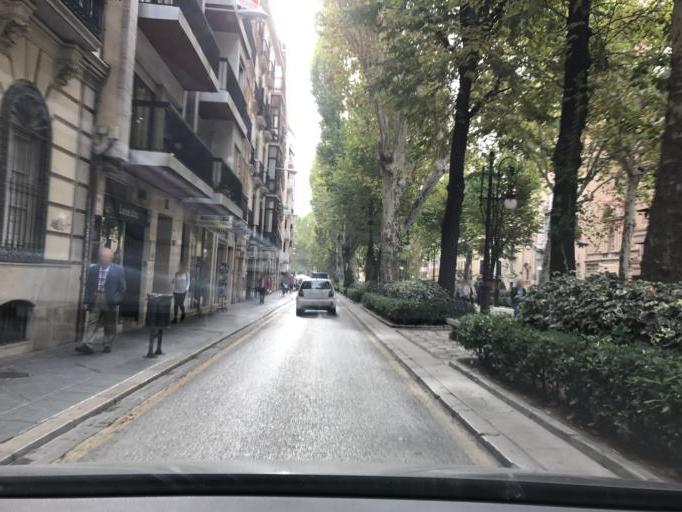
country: ES
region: Andalusia
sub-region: Provincia de Granada
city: Granada
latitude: 37.1709
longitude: -3.5973
